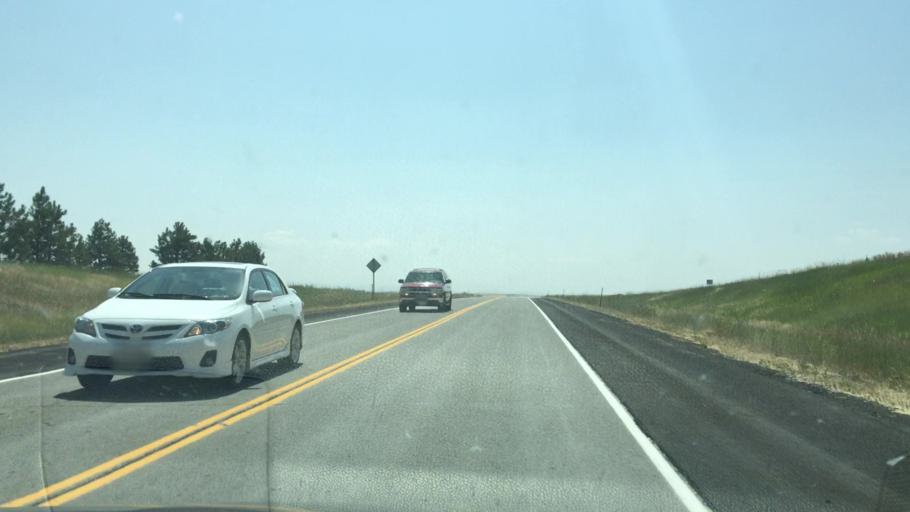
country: US
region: Idaho
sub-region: Lewis County
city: Nezperce
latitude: 46.0946
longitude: -116.3490
